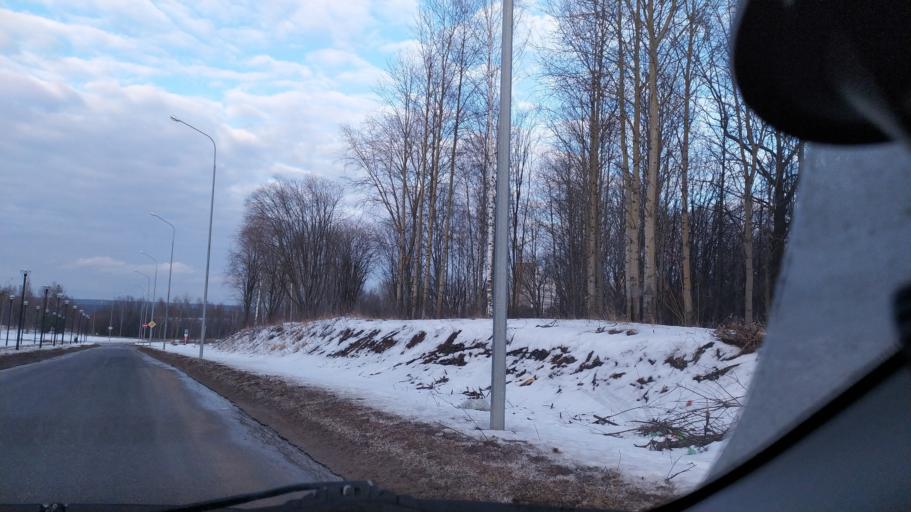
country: RU
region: Chuvashia
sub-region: Cheboksarskiy Rayon
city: Cheboksary
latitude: 56.1506
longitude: 47.2097
